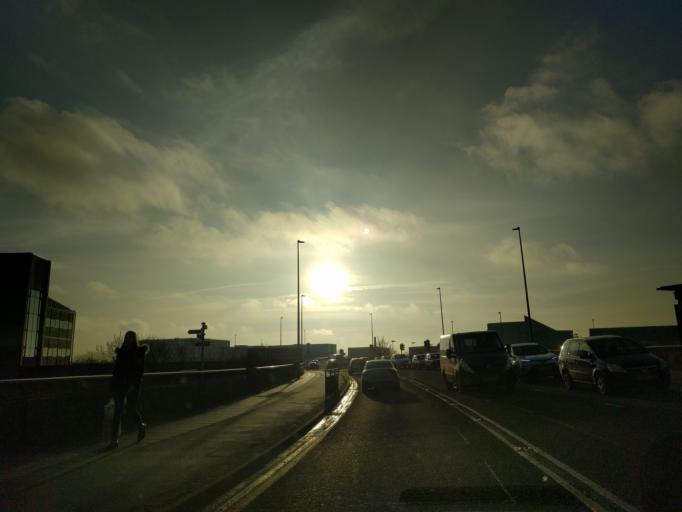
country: GB
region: England
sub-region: Lincolnshire
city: Lincoln
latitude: 53.2298
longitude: -0.5499
